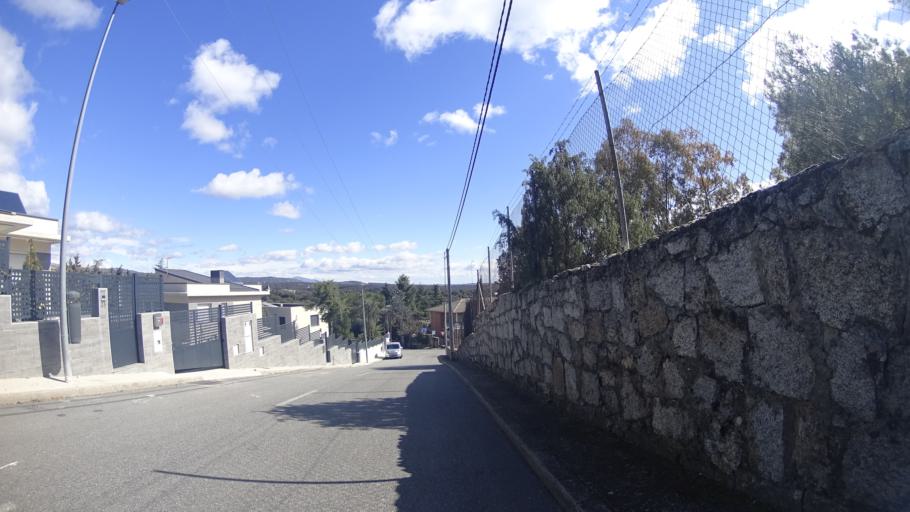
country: ES
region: Madrid
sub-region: Provincia de Madrid
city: Las Matas
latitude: 40.5562
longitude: -3.8927
